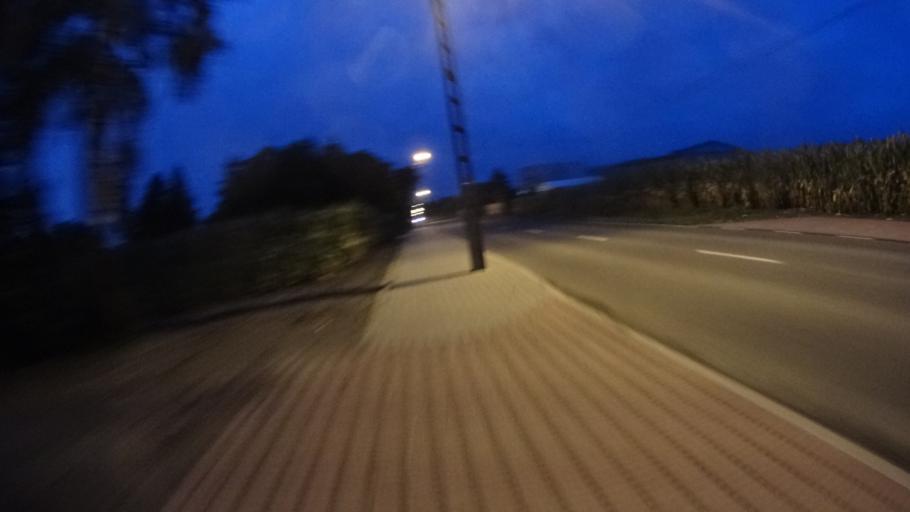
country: PL
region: Masovian Voivodeship
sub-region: Powiat warszawski zachodni
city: Babice
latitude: 52.2254
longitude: 20.8569
